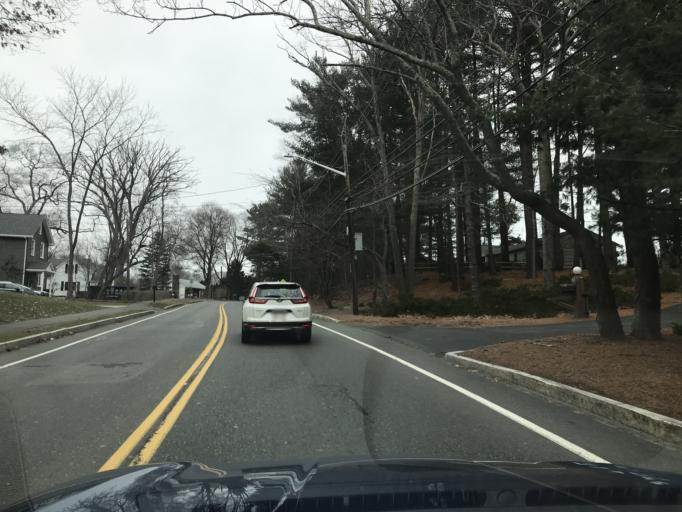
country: US
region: Massachusetts
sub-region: Essex County
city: Lynnfield
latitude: 42.5131
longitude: -71.0179
